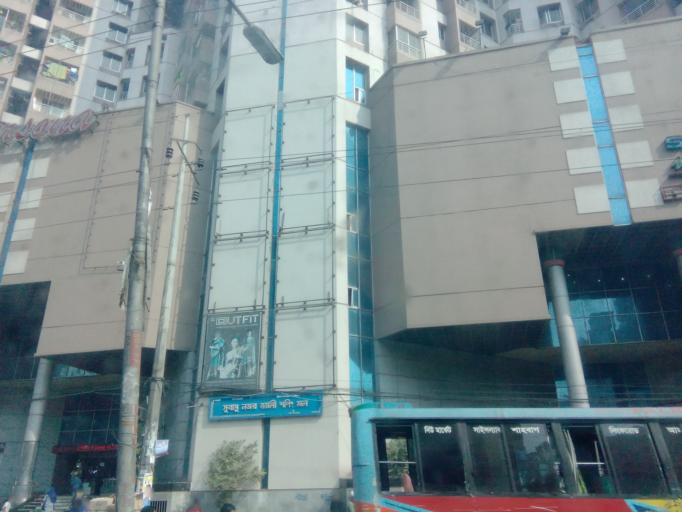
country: BD
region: Dhaka
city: Paltan
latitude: 23.7894
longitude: 90.4252
